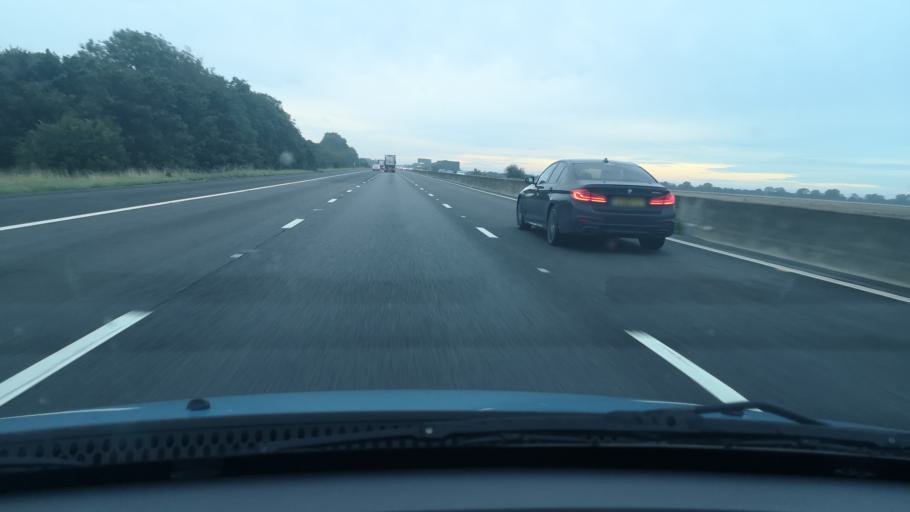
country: GB
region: England
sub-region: East Riding of Yorkshire
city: Rawcliffe
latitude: 53.6634
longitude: -0.9646
